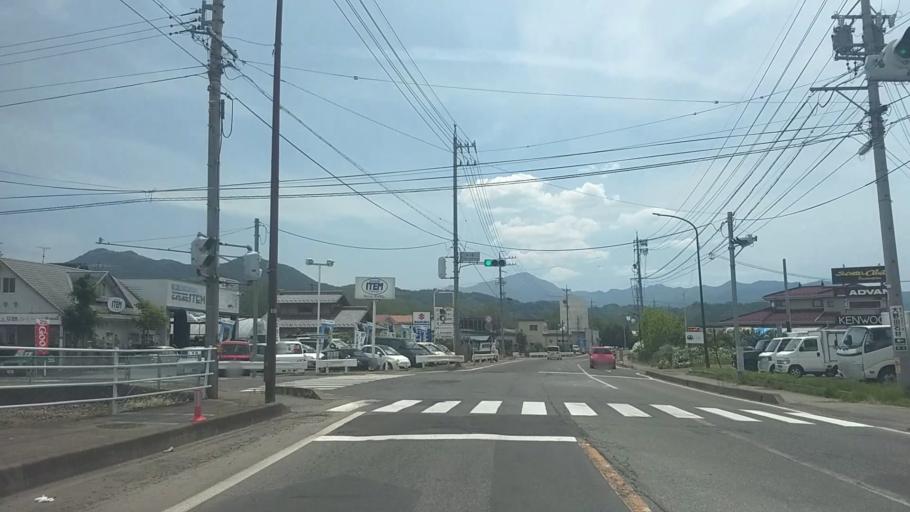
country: JP
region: Nagano
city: Saku
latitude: 36.1784
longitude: 138.4833
